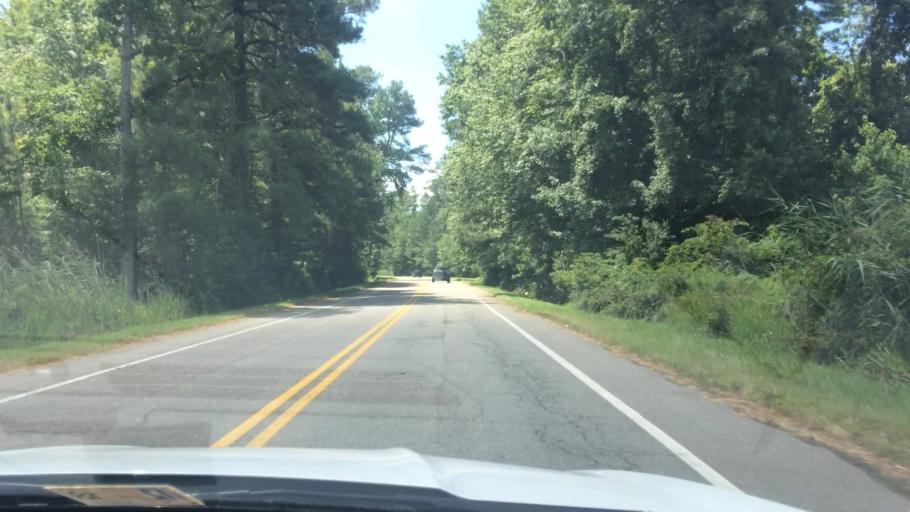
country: US
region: Virginia
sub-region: King William County
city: West Point
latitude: 37.5510
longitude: -76.7938
